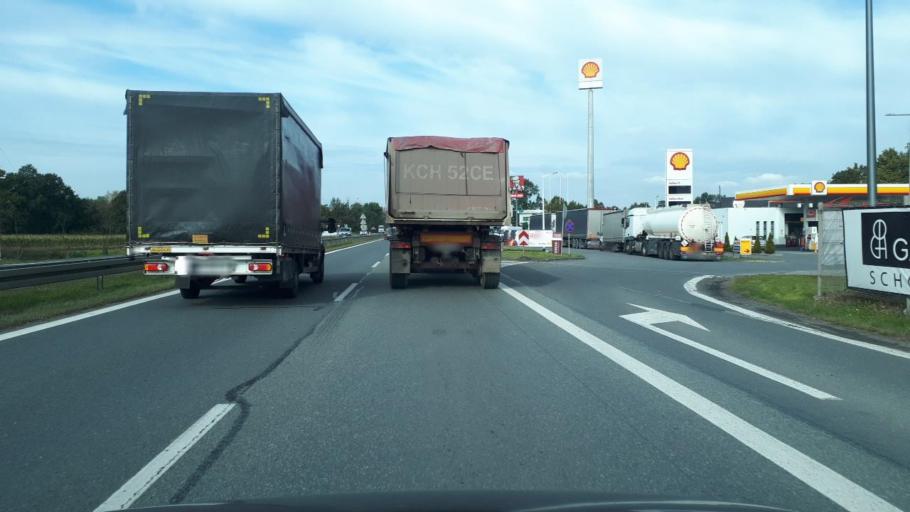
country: PL
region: Silesian Voivodeship
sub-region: Powiat bielski
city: Czechowice-Dziedzice
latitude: 49.9294
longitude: 18.9915
